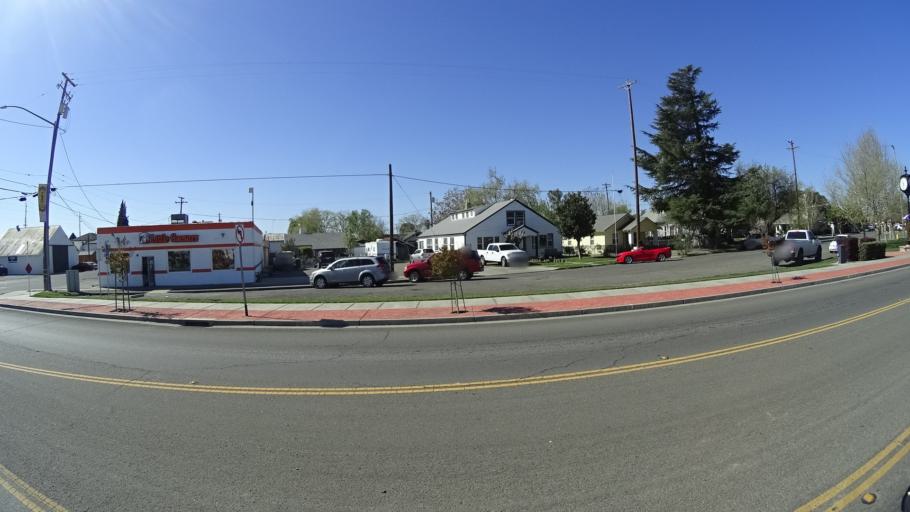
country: US
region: California
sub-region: Glenn County
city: Orland
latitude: 39.7475
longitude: -122.1984
